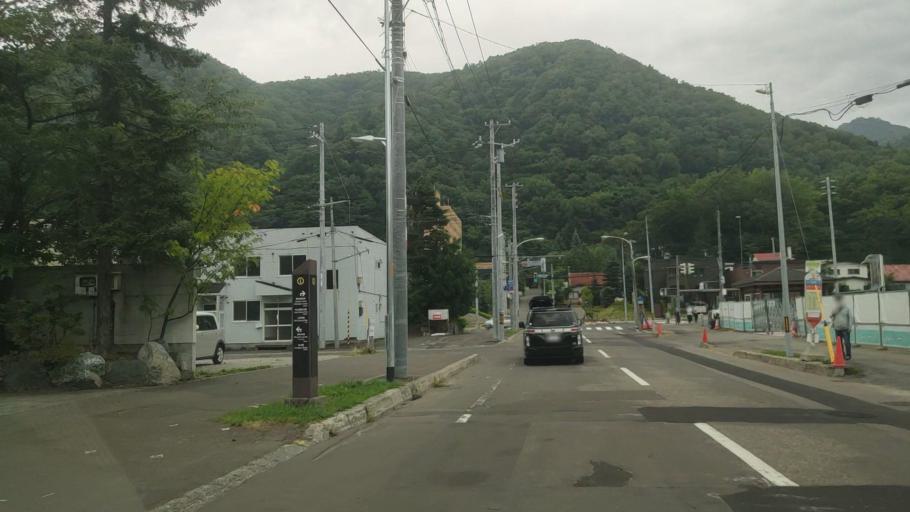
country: JP
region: Hokkaido
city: Sapporo
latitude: 42.9677
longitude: 141.1677
